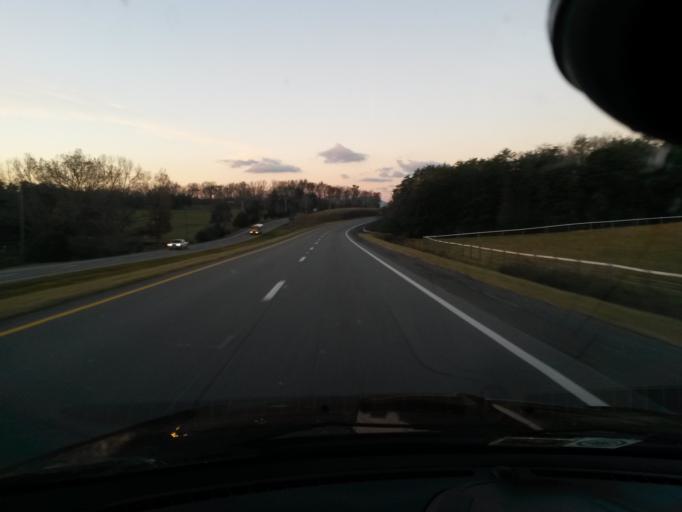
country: US
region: Virginia
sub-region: Botetourt County
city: Fincastle
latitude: 37.5557
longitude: -79.8486
